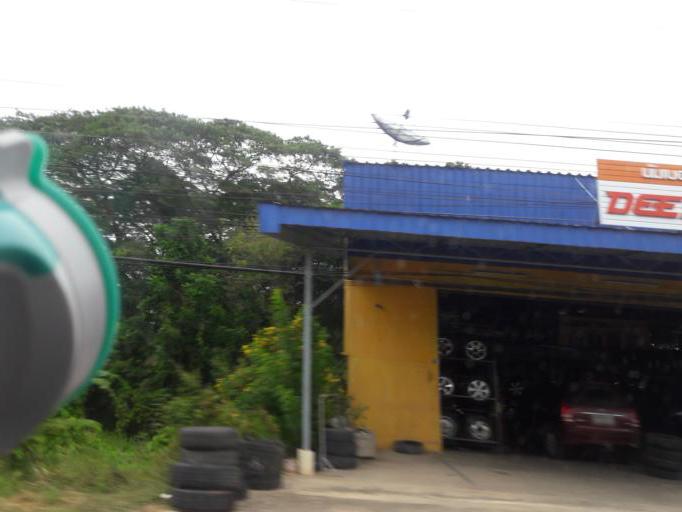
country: TH
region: Ratchaburi
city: Damnoen Saduak
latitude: 13.5654
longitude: 99.9698
